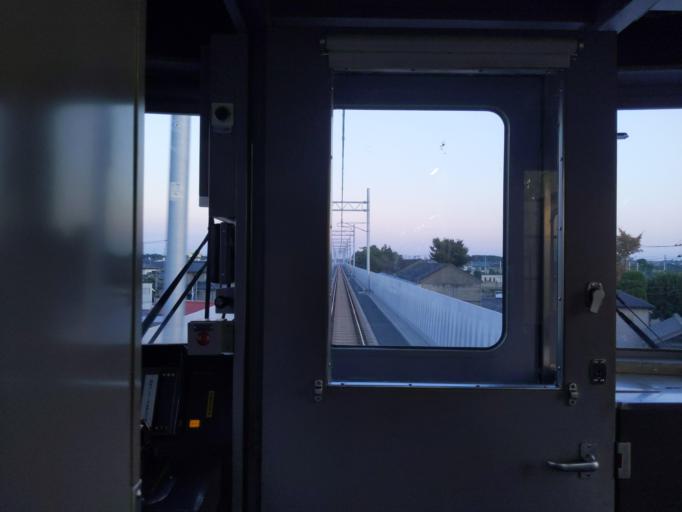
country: JP
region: Chiba
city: Noda
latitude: 35.9418
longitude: 139.8742
